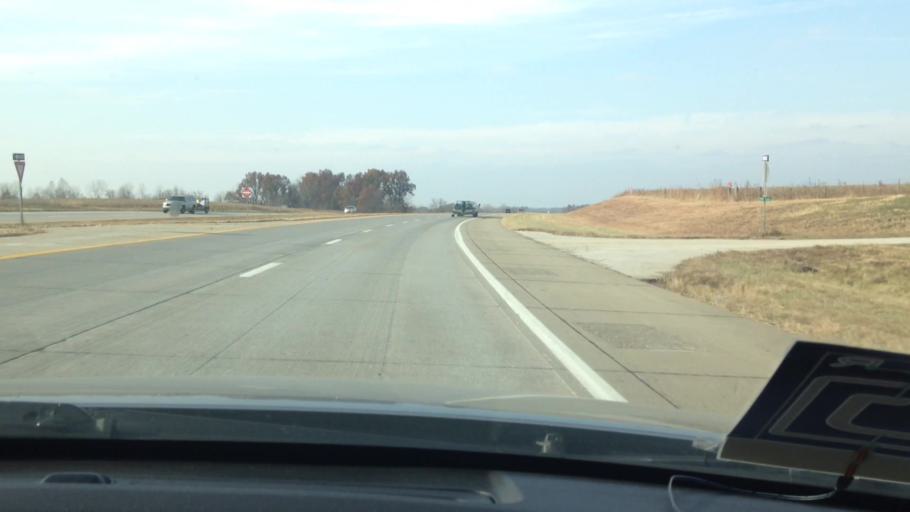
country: US
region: Missouri
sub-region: Henry County
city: Clinton
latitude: 38.4434
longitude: -93.9540
